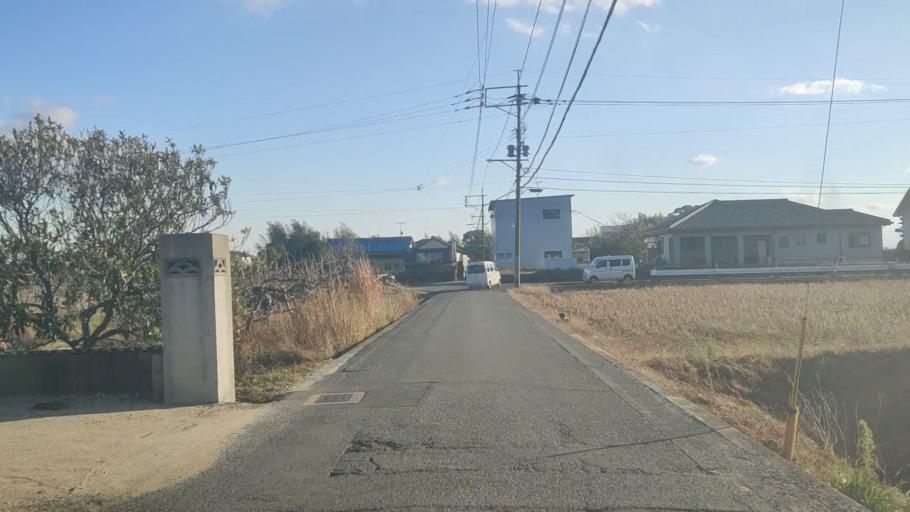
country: JP
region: Saga Prefecture
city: Saga-shi
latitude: 33.2928
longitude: 130.2405
